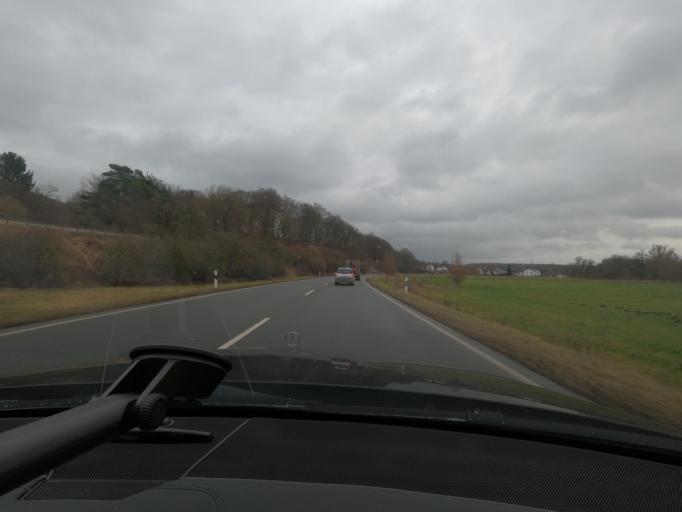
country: DE
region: Hesse
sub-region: Regierungsbezirk Kassel
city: Volkmarsen
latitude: 51.3907
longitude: 9.1419
